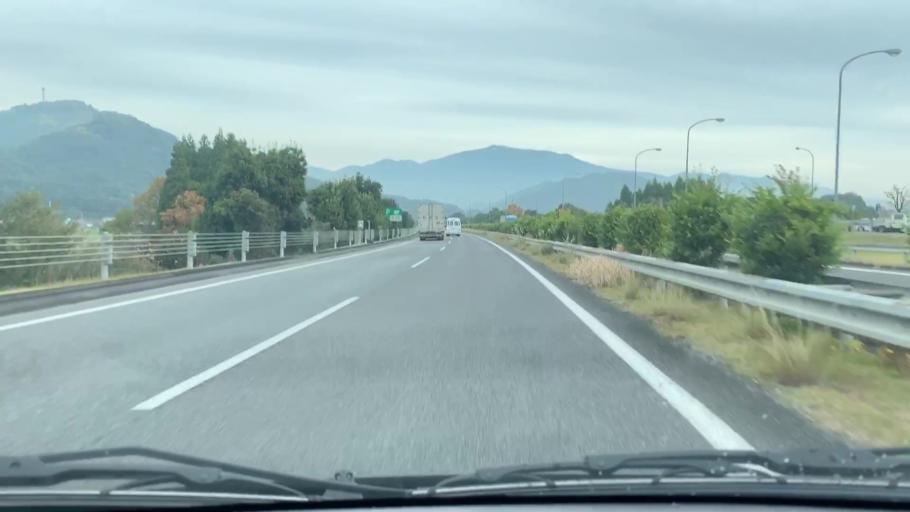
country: JP
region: Saga Prefecture
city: Takeocho-takeo
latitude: 33.2524
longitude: 130.0778
